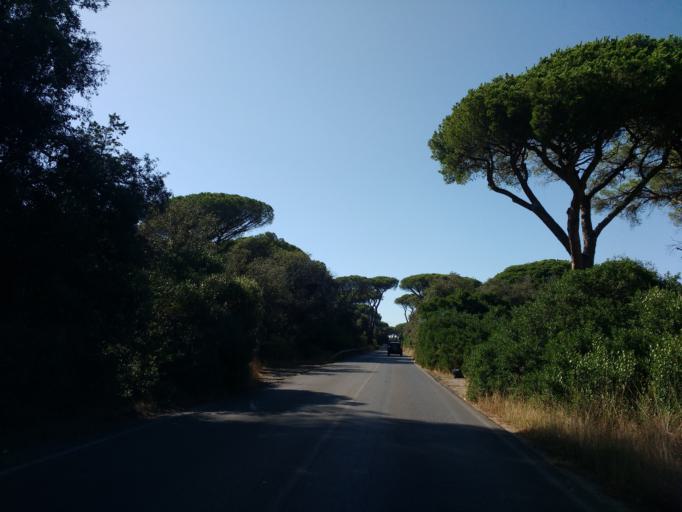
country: IT
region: Latium
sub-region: Citta metropolitana di Roma Capitale
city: Acilia-Castel Fusano-Ostia Antica
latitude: 41.7201
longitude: 12.3485
